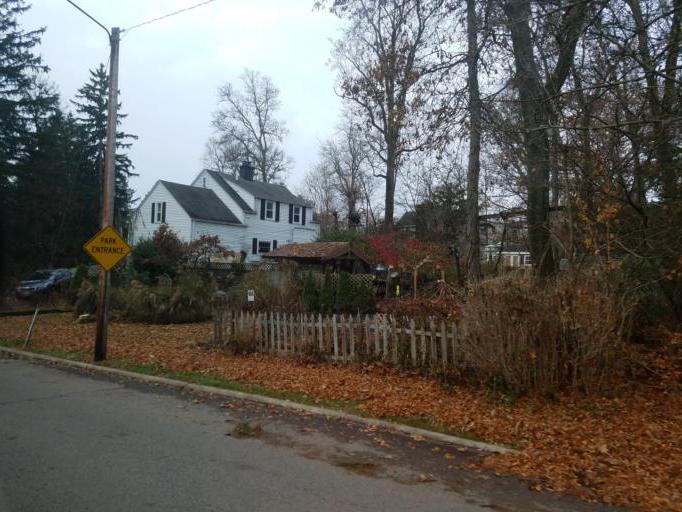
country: US
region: Ohio
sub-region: Richland County
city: Mansfield
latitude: 40.7278
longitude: -82.5332
